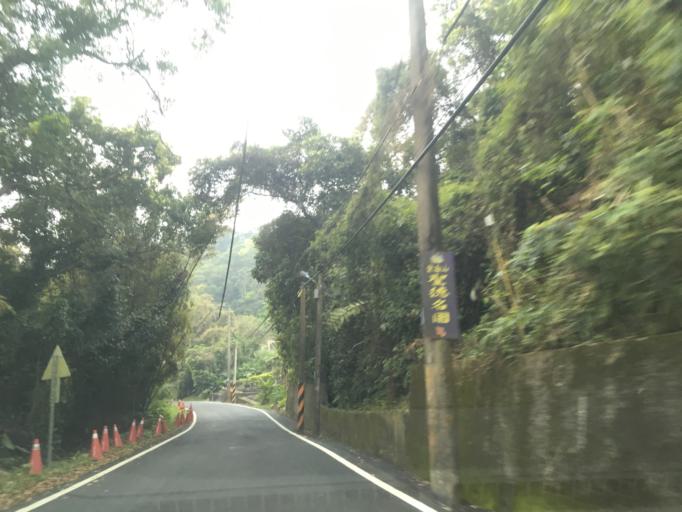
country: TW
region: Taiwan
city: Daxi
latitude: 24.8801
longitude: 121.3063
